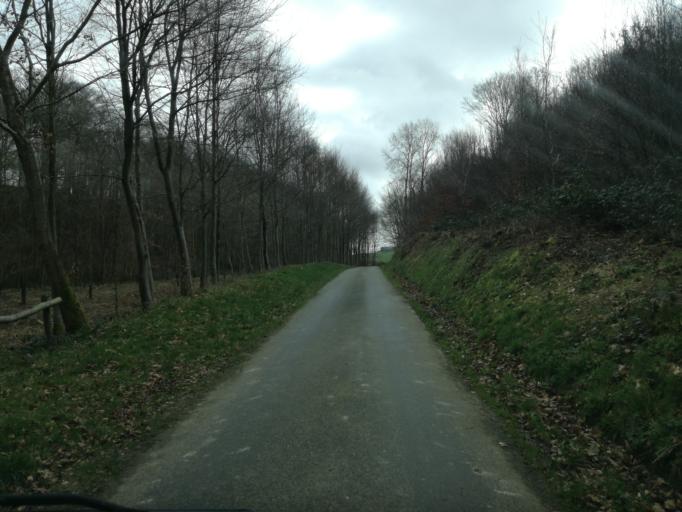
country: FR
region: Haute-Normandie
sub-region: Departement de la Seine-Maritime
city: Yebleron
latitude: 49.6812
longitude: 0.4946
